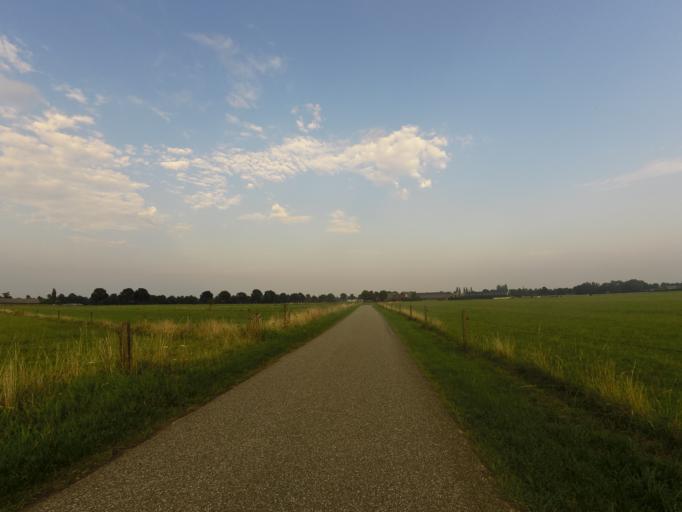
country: NL
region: Gelderland
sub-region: Oude IJsselstreek
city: Gendringen
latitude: 51.8822
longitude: 6.3623
